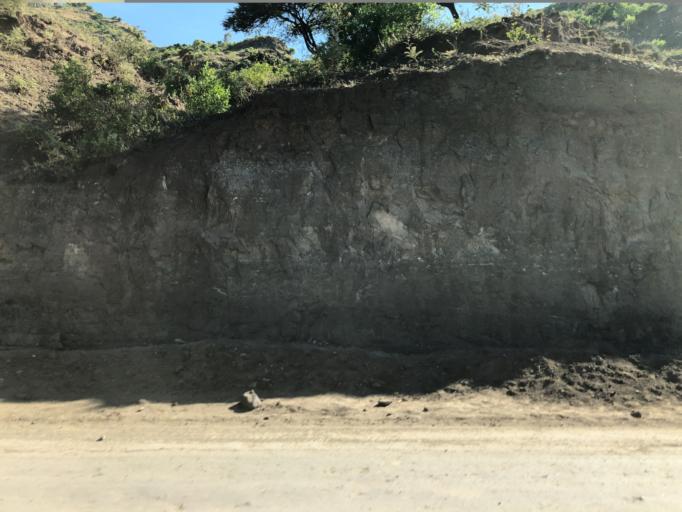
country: ET
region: Amhara
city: Lalibela
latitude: 12.0054
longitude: 39.0575
